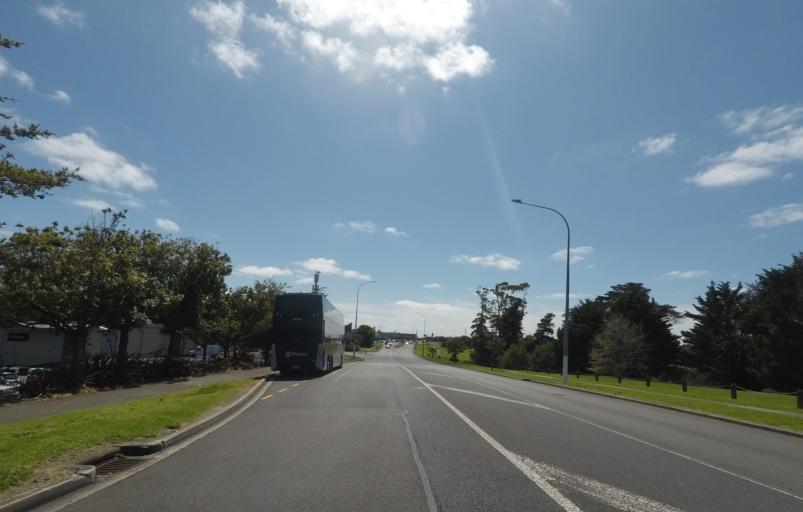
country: NZ
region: Auckland
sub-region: Auckland
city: Pakuranga
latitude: -36.9325
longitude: 174.9153
